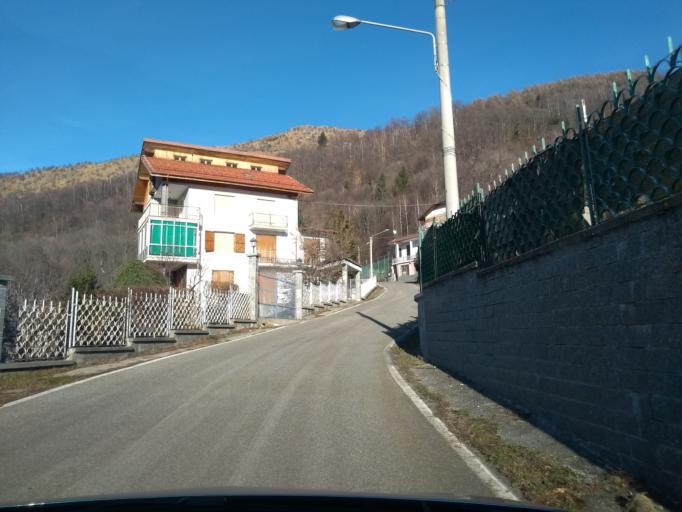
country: IT
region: Piedmont
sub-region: Provincia di Torino
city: Pessinetto
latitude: 45.2848
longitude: 7.4315
